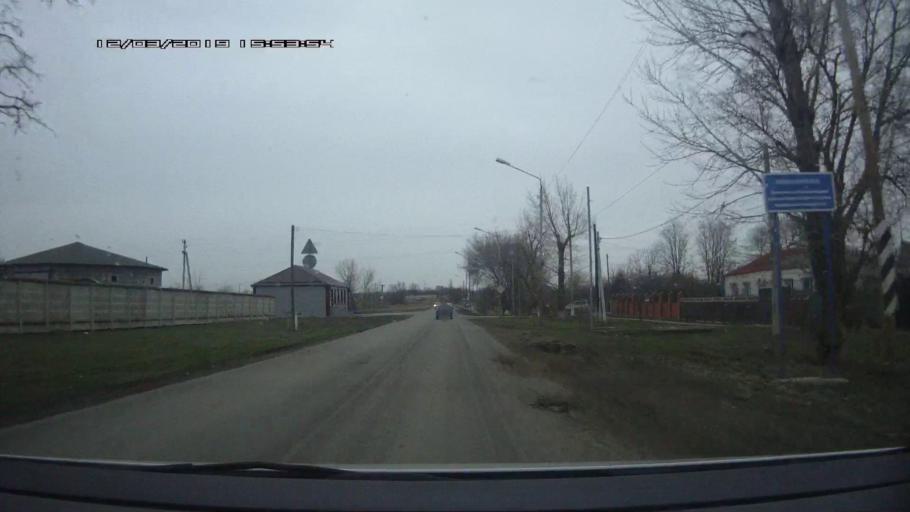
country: RU
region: Rostov
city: Novobataysk
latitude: 46.8874
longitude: 39.7767
